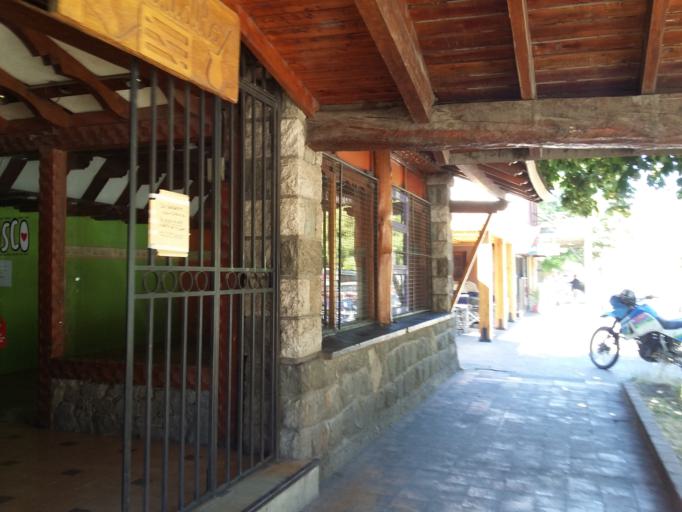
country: AR
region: Neuquen
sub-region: Departamento de Lacar
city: San Martin de los Andes
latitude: -40.1555
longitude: -71.3463
